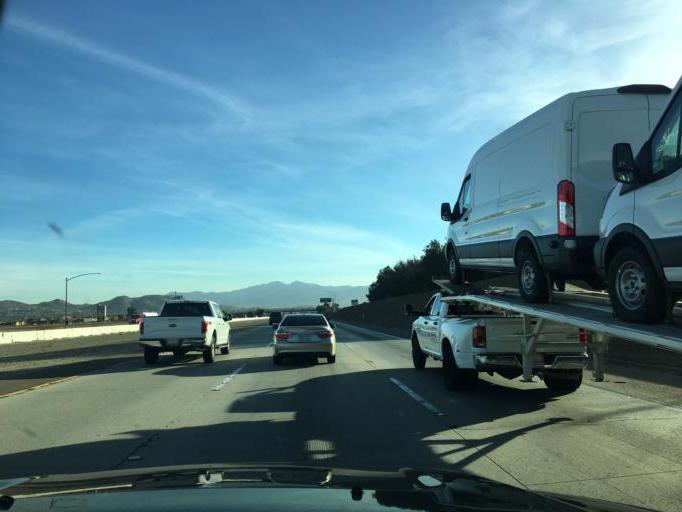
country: US
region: California
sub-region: Riverside County
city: Mira Loma
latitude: 33.9812
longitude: -117.5491
